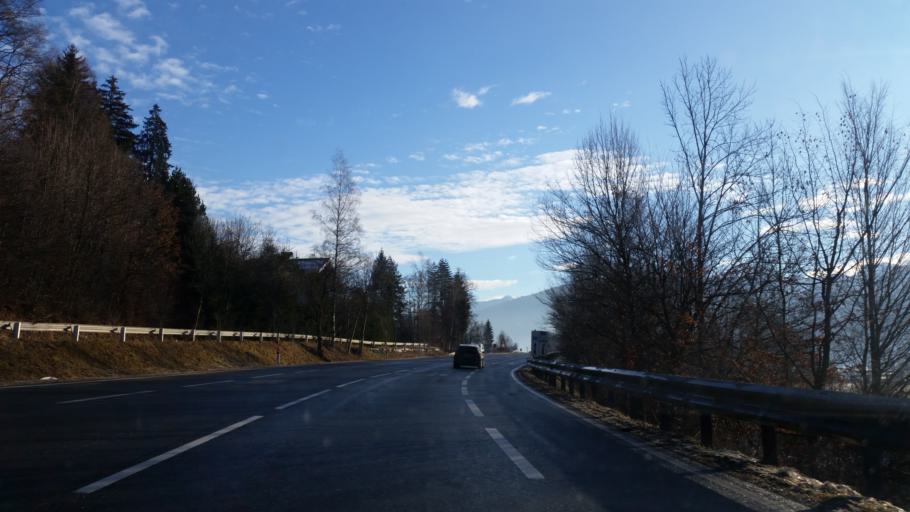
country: AT
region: Salzburg
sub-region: Politischer Bezirk Sankt Johann im Pongau
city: Altenmarkt im Pongau
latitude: 47.3850
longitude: 13.4255
